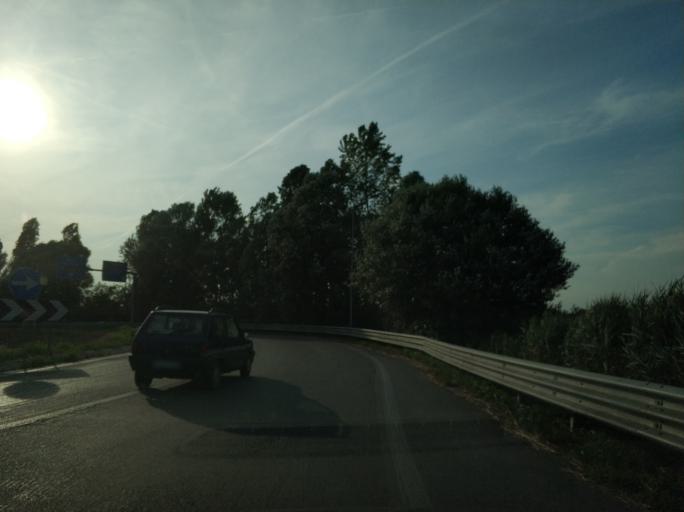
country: IT
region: Veneto
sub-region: Provincia di Padova
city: Arre
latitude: 45.2125
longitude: 11.9035
